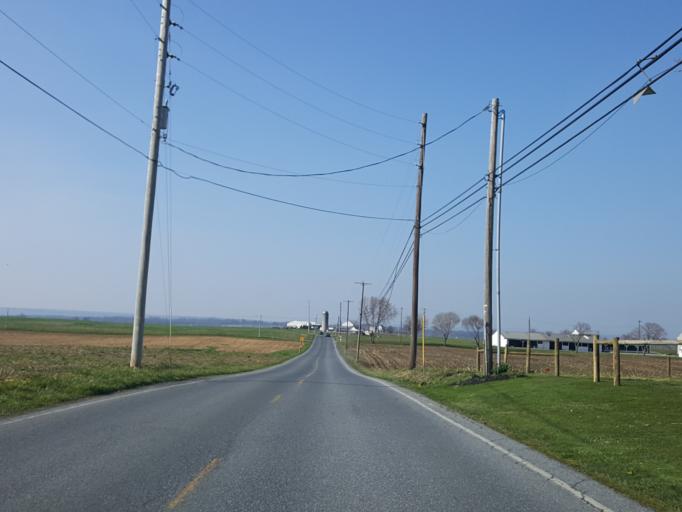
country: US
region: Pennsylvania
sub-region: Lebanon County
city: Annville
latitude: 40.2895
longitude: -76.5219
